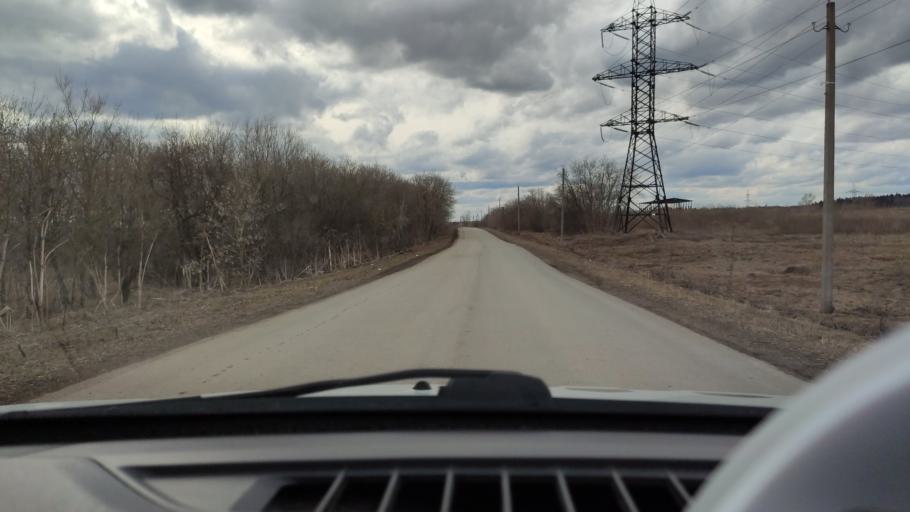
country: RU
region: Perm
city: Froly
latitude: 57.9298
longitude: 56.2485
